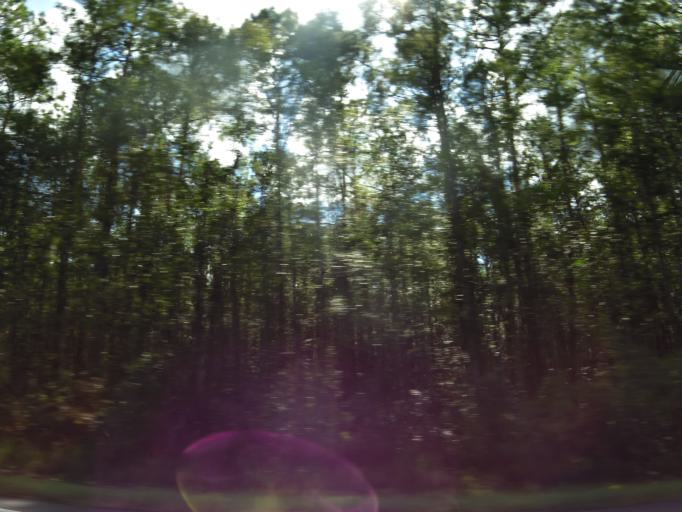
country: US
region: Georgia
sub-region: Echols County
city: Statenville
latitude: 30.7388
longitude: -83.0951
